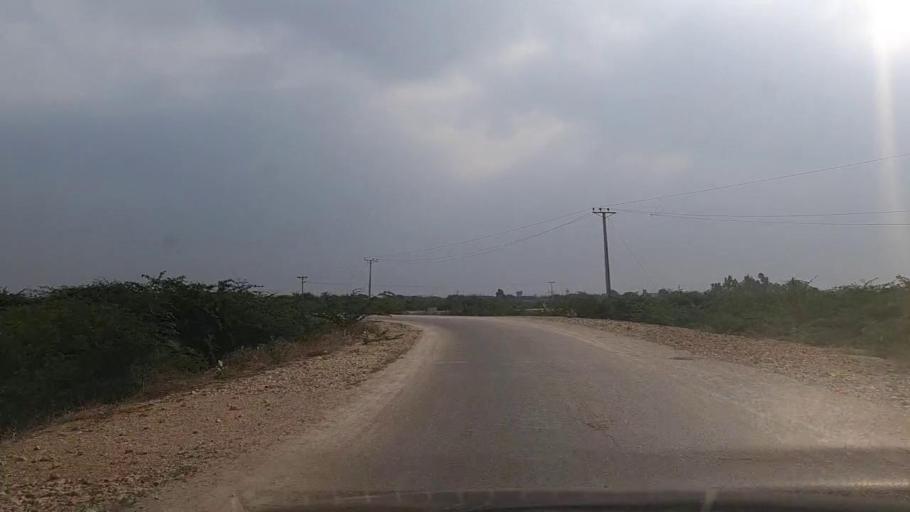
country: PK
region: Sindh
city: Thatta
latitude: 24.8523
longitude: 67.7775
